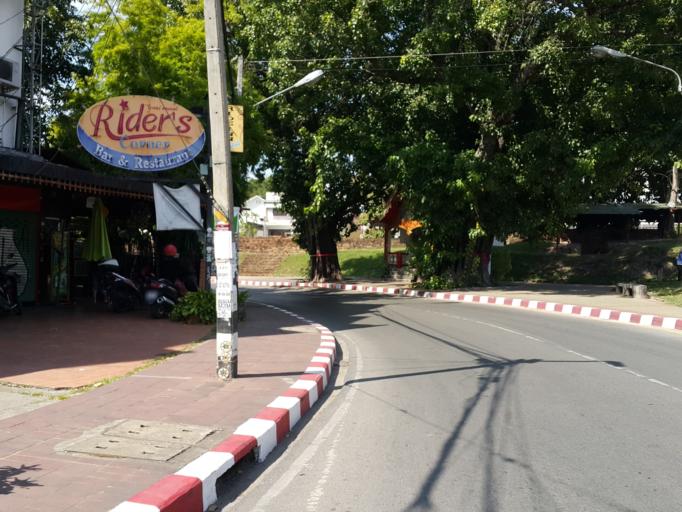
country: TH
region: Chiang Mai
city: Chiang Mai
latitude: 18.7946
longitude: 98.9935
